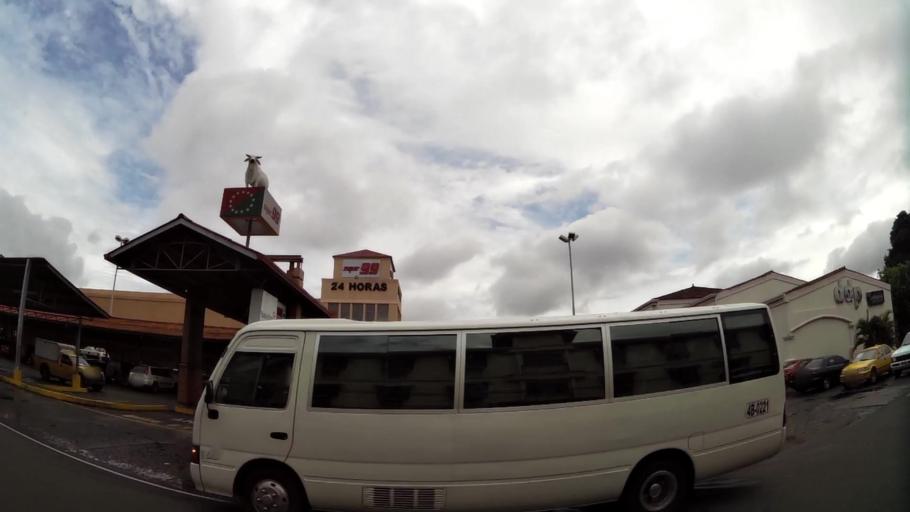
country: PA
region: Chiriqui
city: David
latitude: 8.4273
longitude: -82.4371
